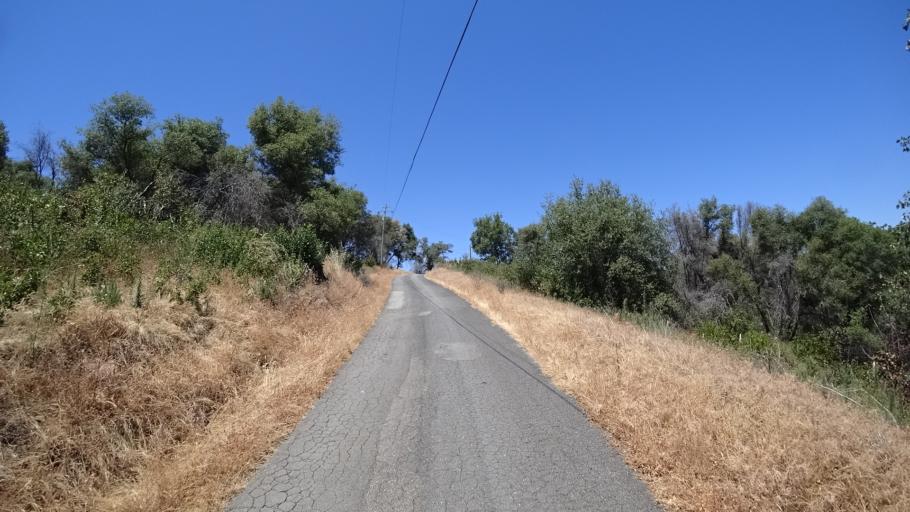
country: US
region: California
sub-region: Calaveras County
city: Mountain Ranch
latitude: 38.2785
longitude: -120.5950
